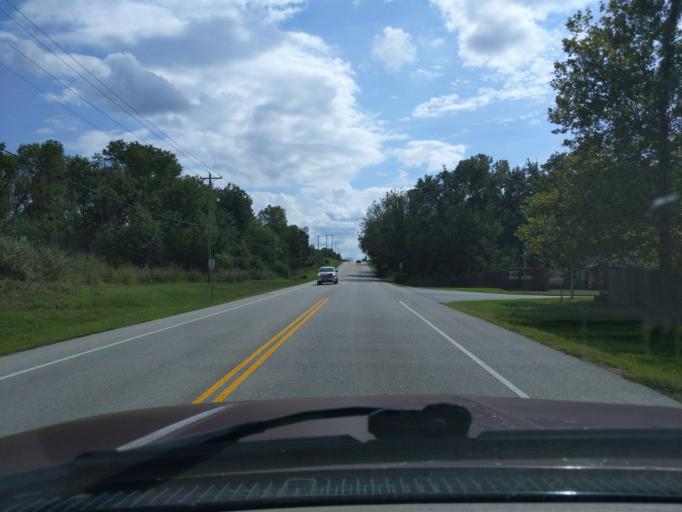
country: US
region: Oklahoma
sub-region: Tulsa County
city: Oakhurst
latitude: 36.0686
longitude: -96.0117
